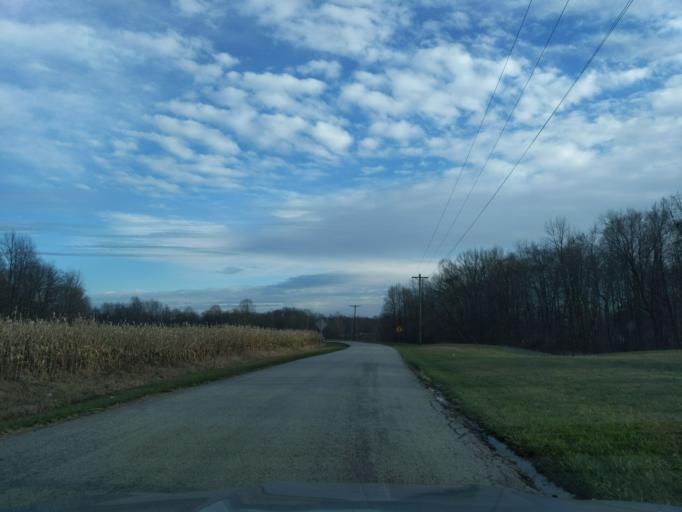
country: US
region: Indiana
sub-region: Decatur County
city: Greensburg
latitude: 39.2142
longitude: -85.4488
